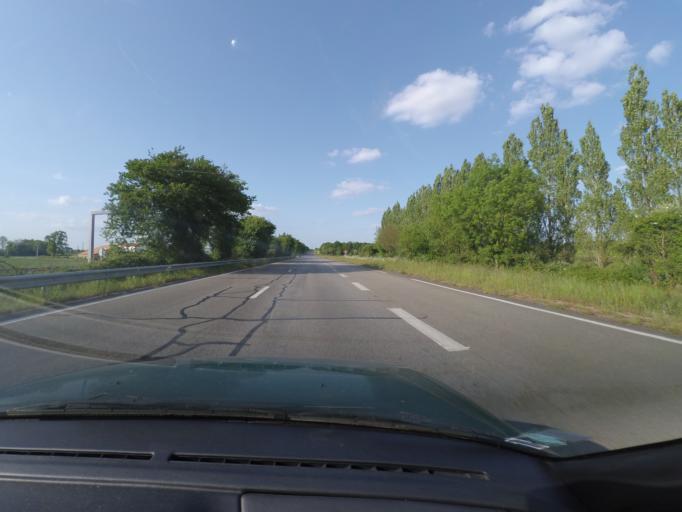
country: FR
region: Pays de la Loire
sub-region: Departement de la Vendee
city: Saligny
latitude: 46.8579
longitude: -1.4080
